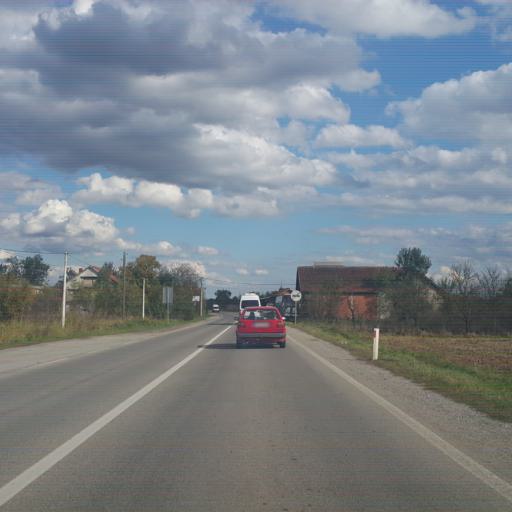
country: RS
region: Central Serbia
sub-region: Rasinski Okrug
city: Aleksandrovac
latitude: 43.5771
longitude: 21.1650
